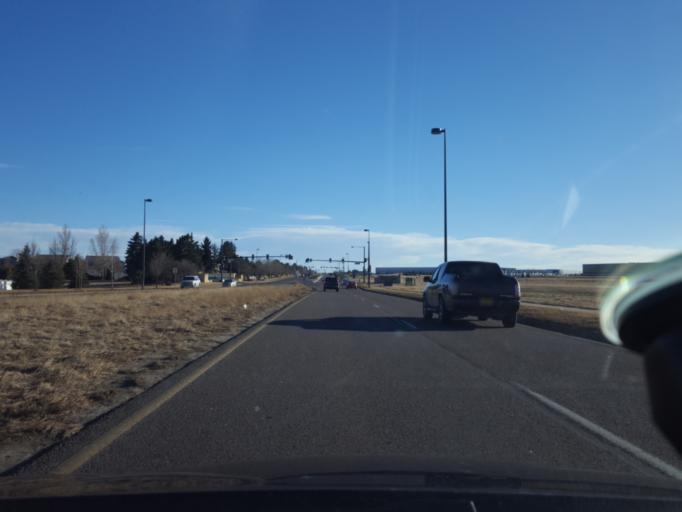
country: US
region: Colorado
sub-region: Adams County
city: Aurora
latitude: 39.7798
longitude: -104.7722
